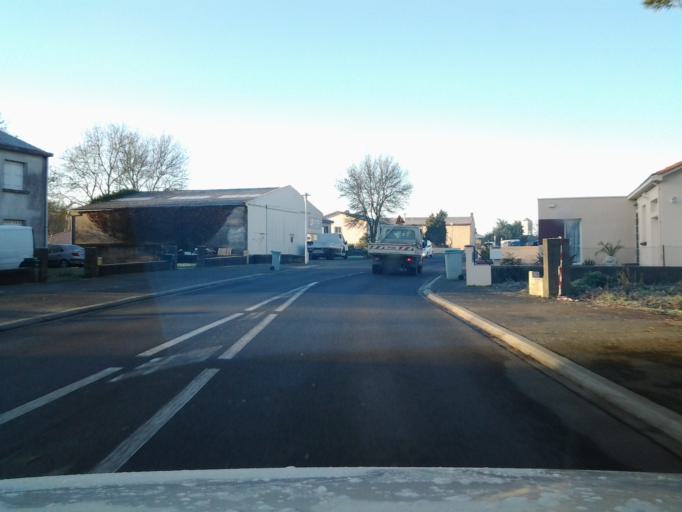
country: FR
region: Pays de la Loire
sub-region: Departement de la Vendee
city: Treize-Septiers
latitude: 46.9872
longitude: -1.2266
